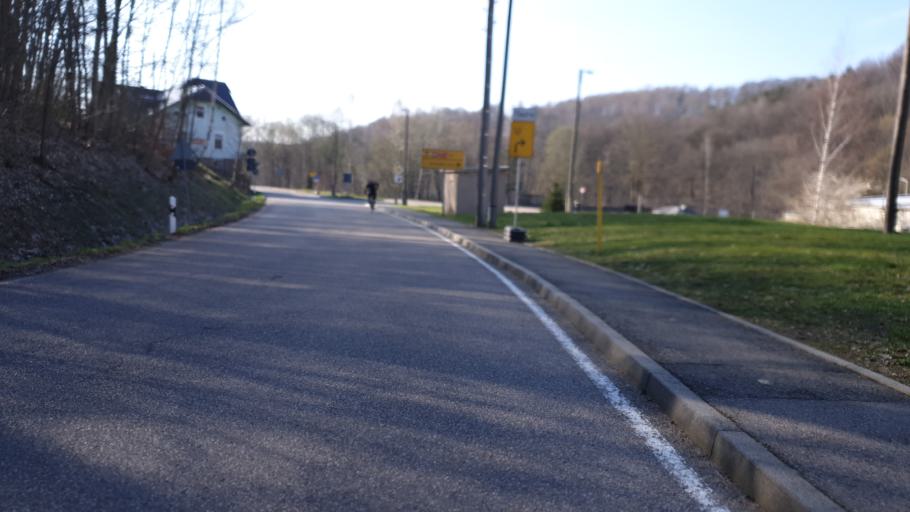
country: DE
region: Saxony
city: Taura
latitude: 50.9432
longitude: 12.8264
